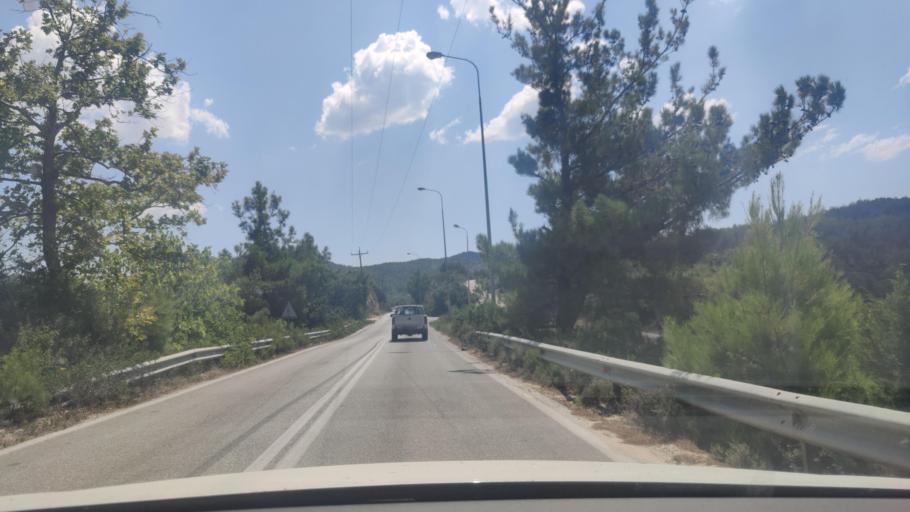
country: GR
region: East Macedonia and Thrace
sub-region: Nomos Kavalas
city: Limenaria
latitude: 40.6417
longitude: 24.5201
